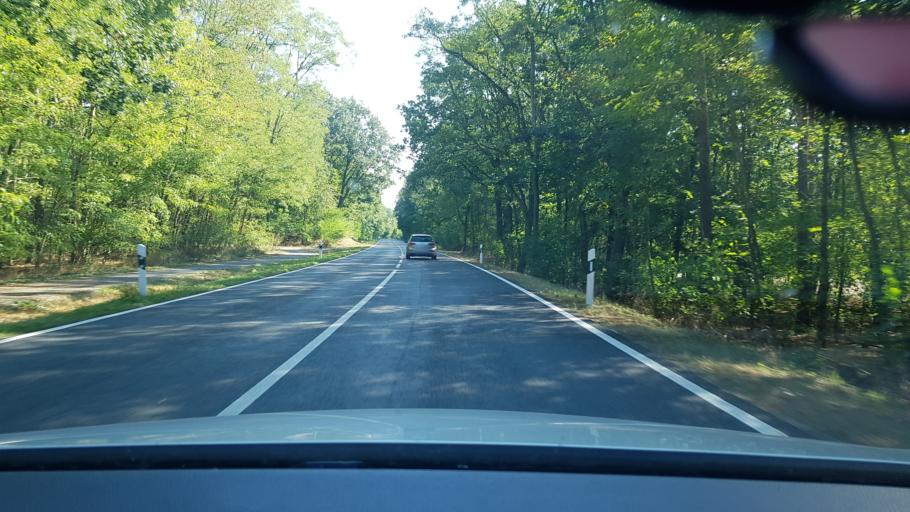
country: DE
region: Brandenburg
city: Mixdorf
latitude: 52.1355
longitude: 14.4360
